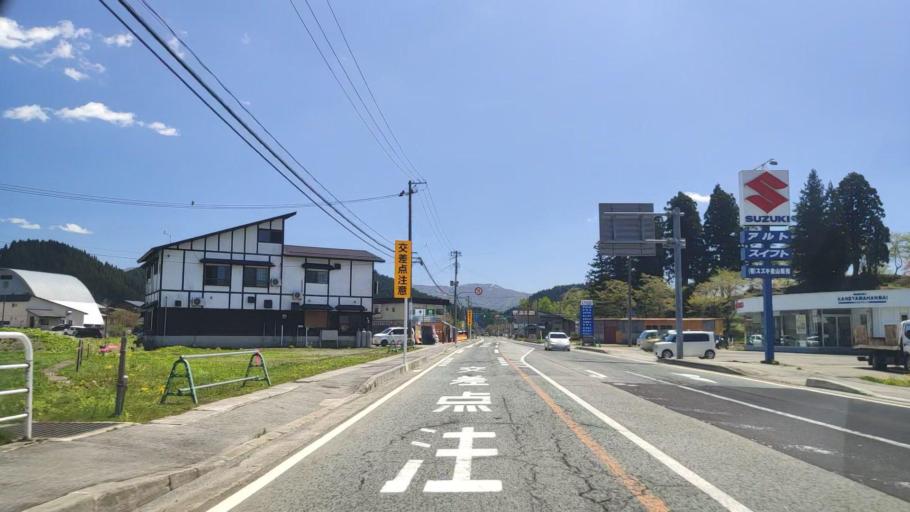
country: JP
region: Yamagata
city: Shinjo
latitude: 38.8879
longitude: 140.3323
